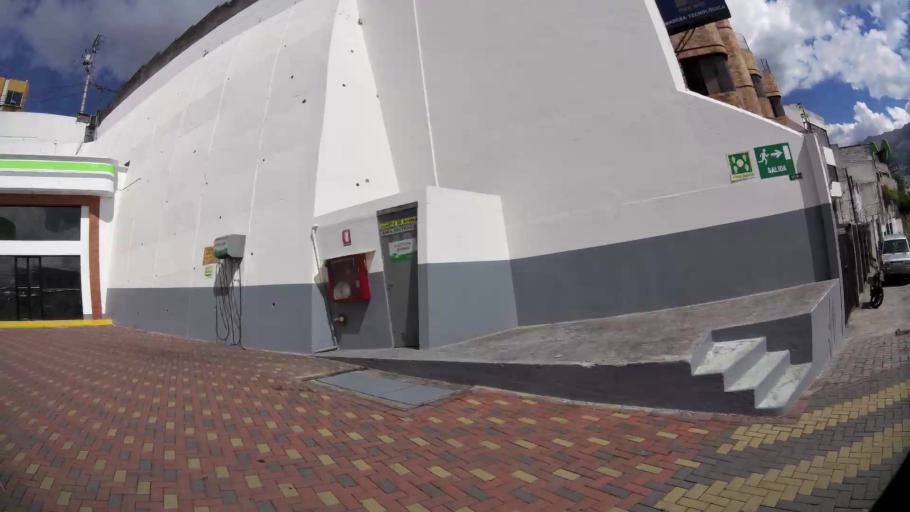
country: EC
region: Pichincha
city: Quito
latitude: -0.1023
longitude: -78.4868
